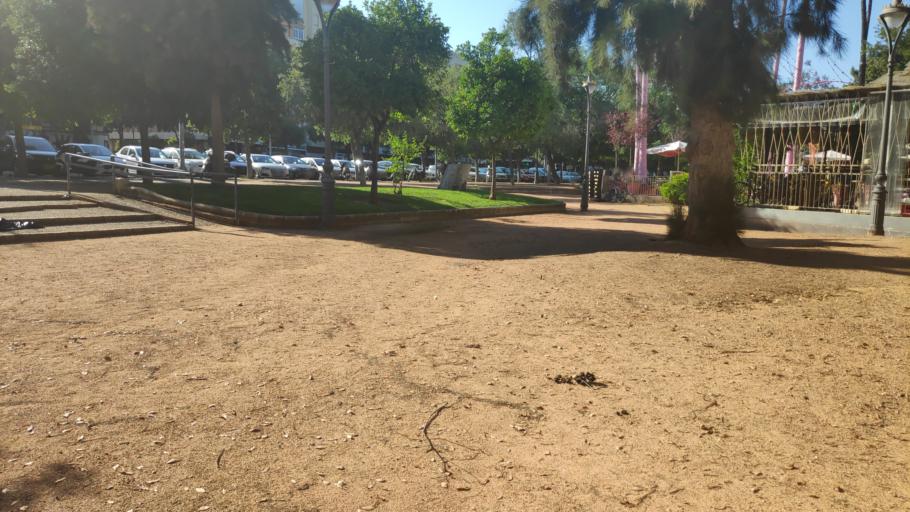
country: ES
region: Andalusia
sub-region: Province of Cordoba
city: Cordoba
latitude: 37.8835
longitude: -4.7857
